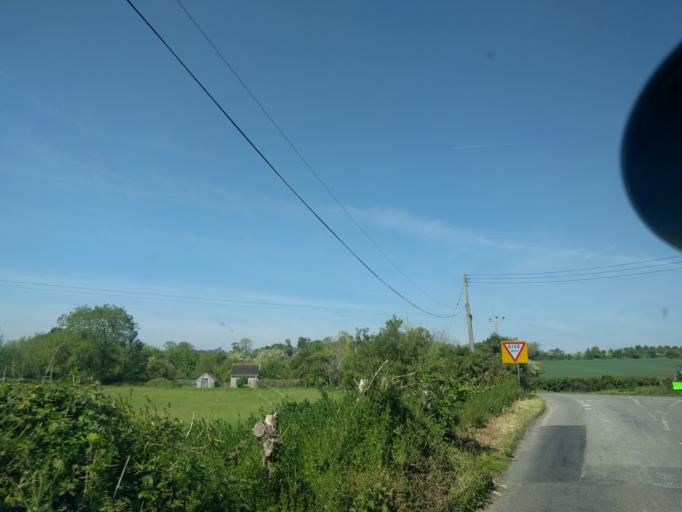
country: GB
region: England
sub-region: Somerset
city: Langport
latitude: 51.0443
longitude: -2.7982
